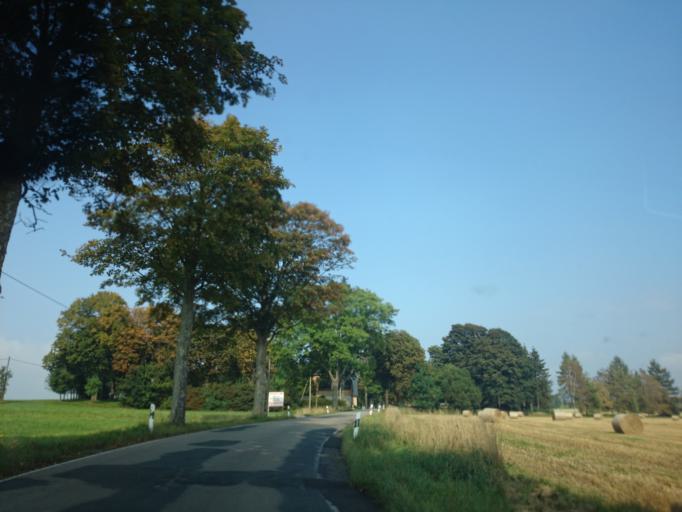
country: DE
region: Saxony
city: Eppendorf
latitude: 50.8194
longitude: 13.2694
